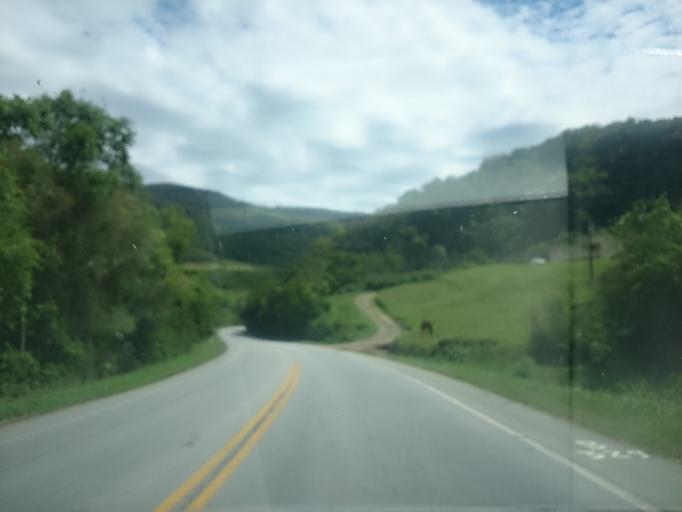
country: BR
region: Santa Catarina
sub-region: Anitapolis
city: Anitapolis
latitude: -27.7116
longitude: -49.2573
